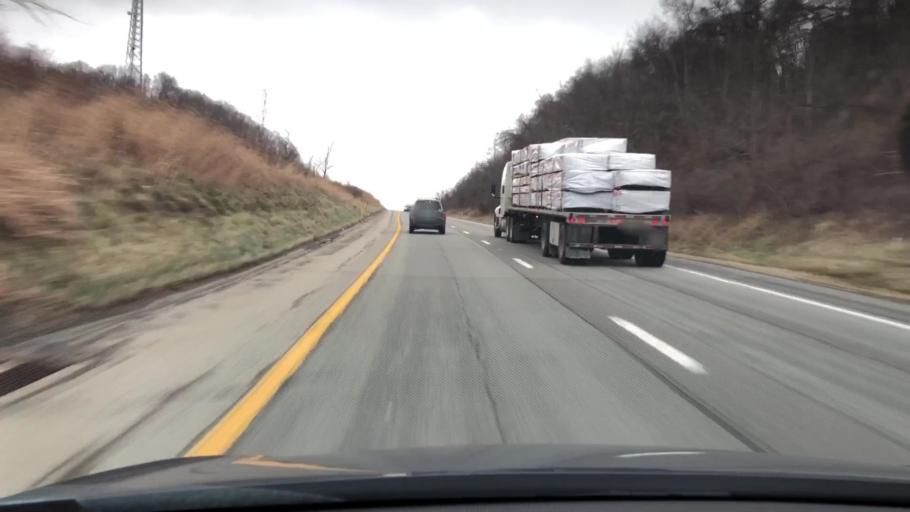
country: US
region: Pennsylvania
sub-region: Washington County
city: East Washington
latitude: 40.0789
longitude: -80.1925
